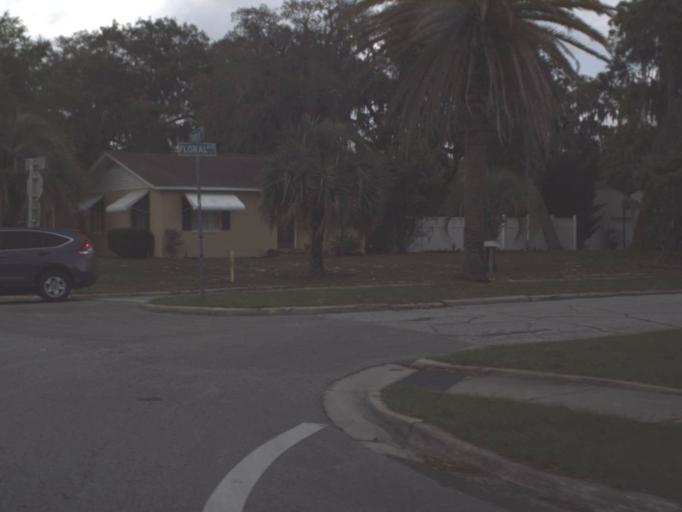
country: US
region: Florida
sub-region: Lake County
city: Eustis
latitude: 28.8592
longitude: -81.6836
